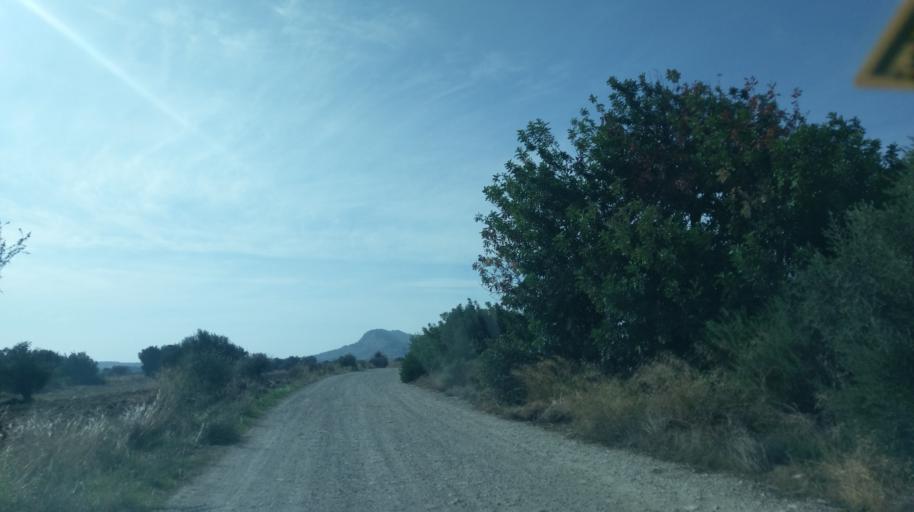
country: CY
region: Ammochostos
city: Trikomo
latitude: 35.3387
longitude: 33.8471
